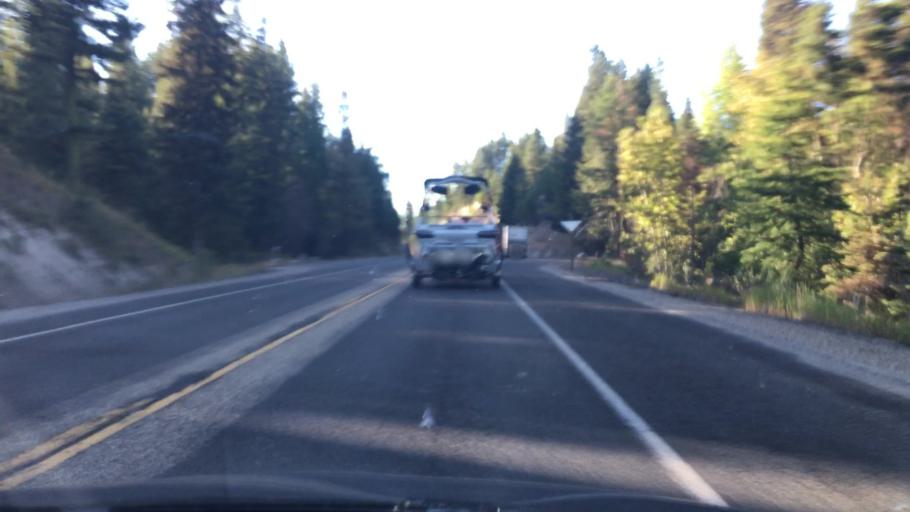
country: US
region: Idaho
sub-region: Valley County
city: Cascade
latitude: 44.5762
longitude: -116.0341
